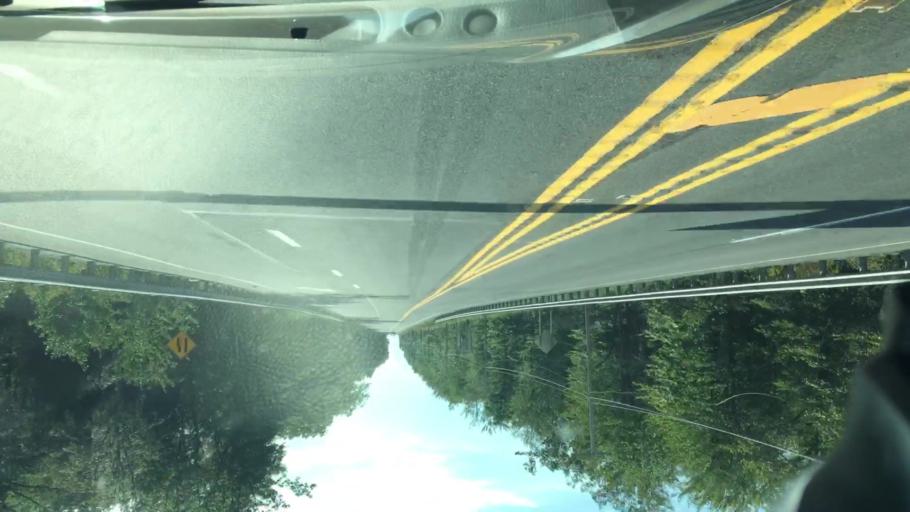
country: US
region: Pennsylvania
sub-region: Carbon County
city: Towamensing Trails
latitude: 40.9815
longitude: -75.6318
